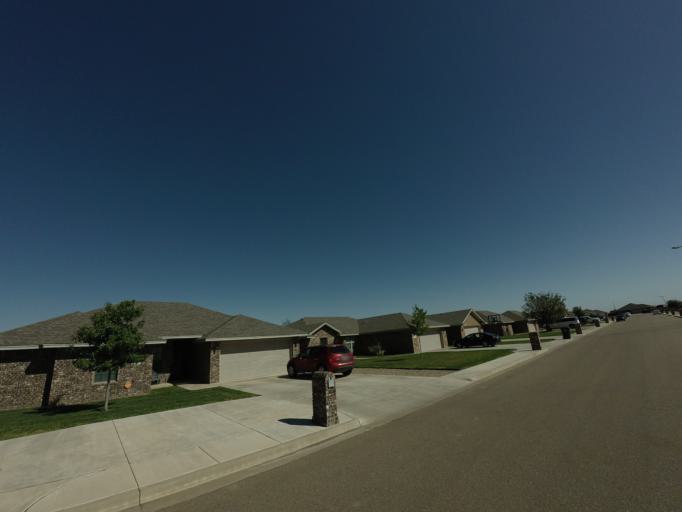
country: US
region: New Mexico
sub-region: Curry County
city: Clovis
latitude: 34.4217
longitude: -103.1592
